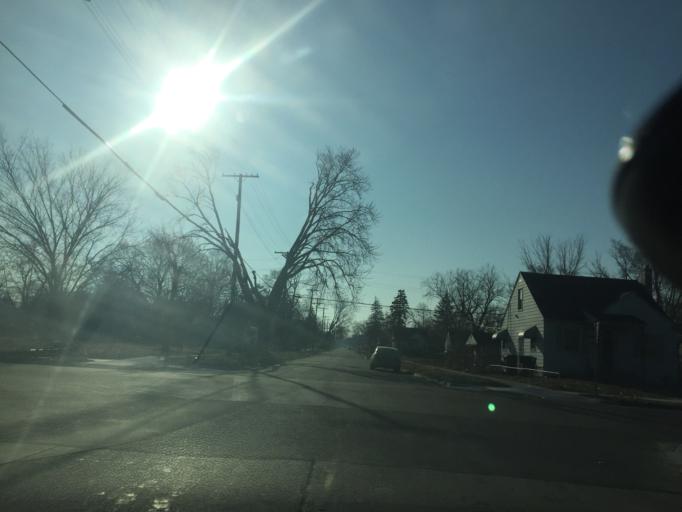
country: US
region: Michigan
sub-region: Macomb County
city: Eastpointe
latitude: 42.4402
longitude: -82.9584
